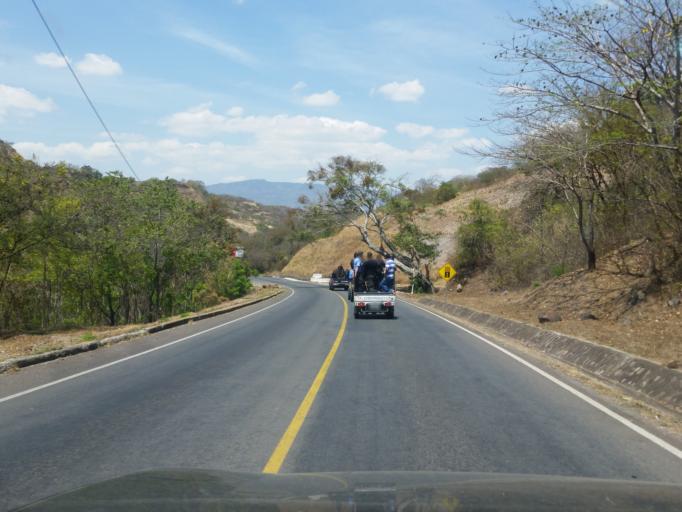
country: NI
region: Esteli
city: Esteli
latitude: 13.0527
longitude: -86.3273
